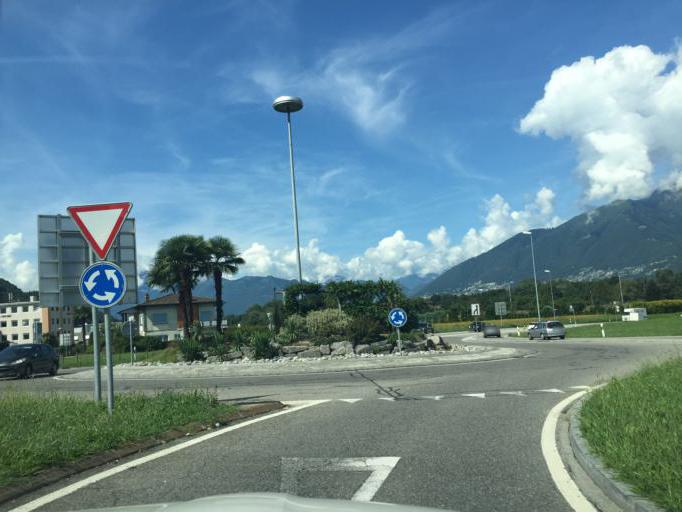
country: CH
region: Ticino
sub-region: Locarno District
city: Cugnasco
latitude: 46.1531
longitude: 8.8930
